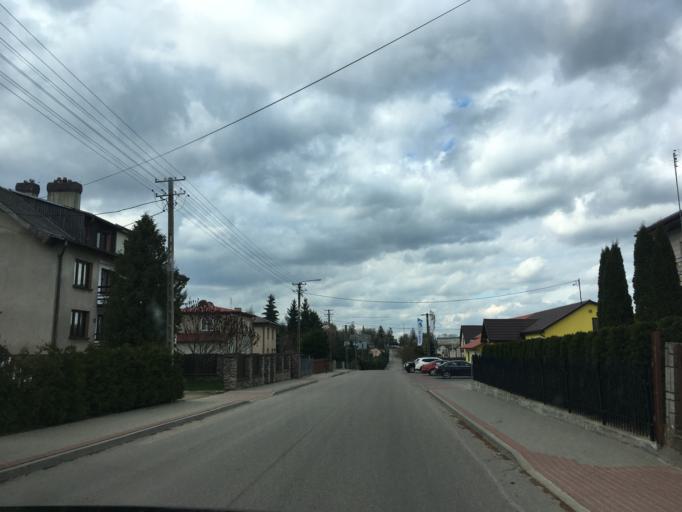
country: PL
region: Podlasie
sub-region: Suwalki
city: Suwalki
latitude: 54.3636
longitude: 22.8687
